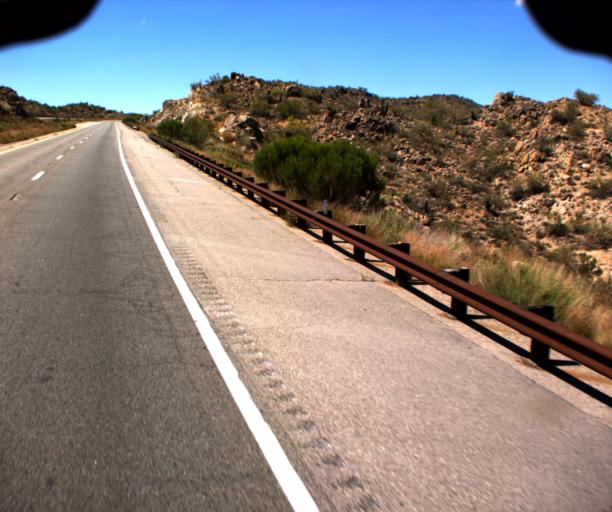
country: US
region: Arizona
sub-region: Yavapai County
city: Bagdad
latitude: 34.4494
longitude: -113.2845
